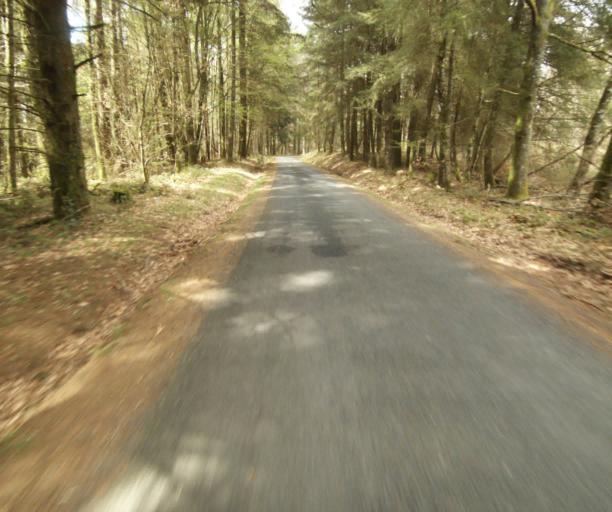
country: FR
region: Limousin
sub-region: Departement de la Correze
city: Argentat
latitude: 45.1954
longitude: 1.9097
